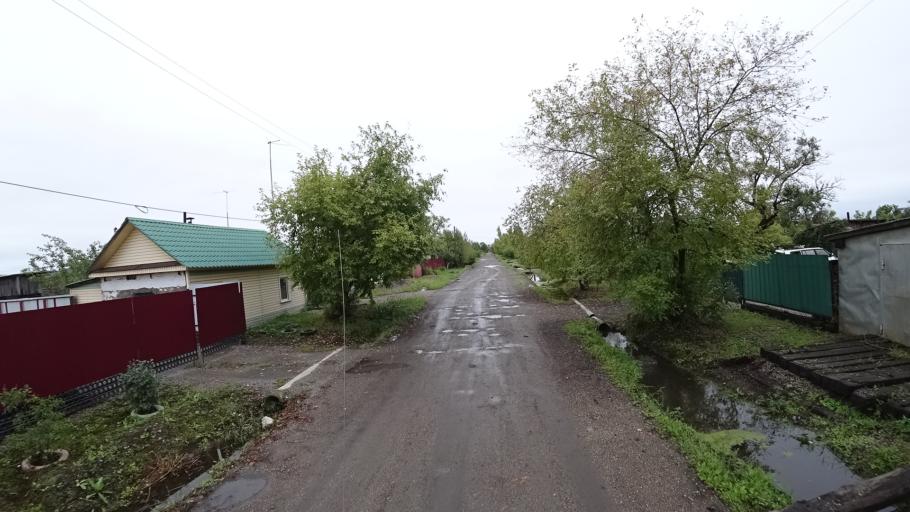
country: RU
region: Primorskiy
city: Monastyrishche
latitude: 44.2115
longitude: 132.4323
